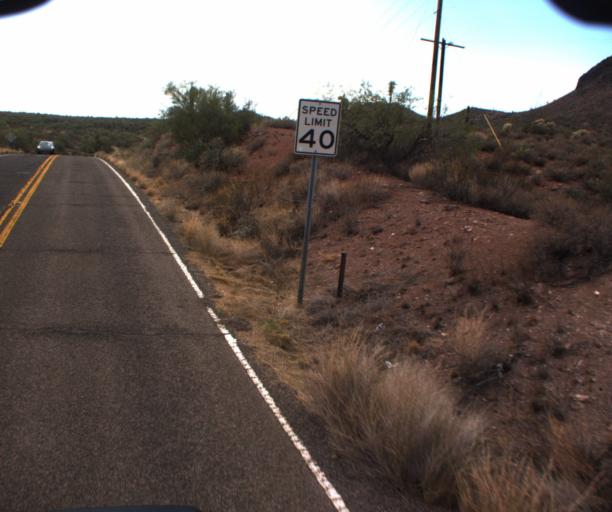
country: US
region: Arizona
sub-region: Pinal County
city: Apache Junction
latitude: 33.4991
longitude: -111.4629
